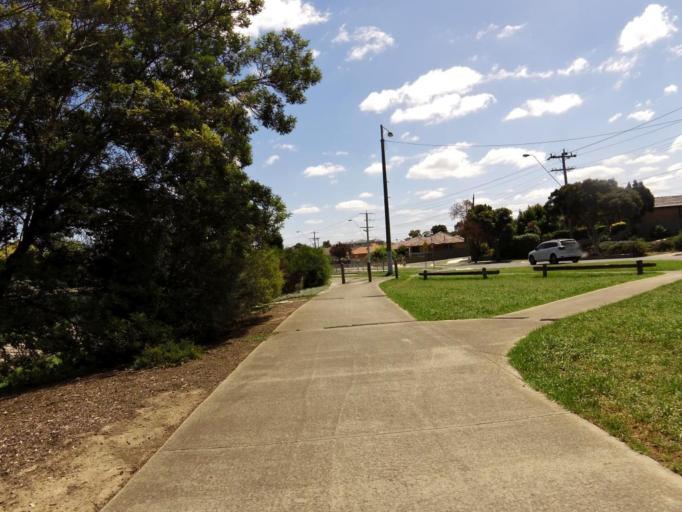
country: AU
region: Victoria
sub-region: Whittlesea
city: Lalor
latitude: -37.6714
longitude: 145.0102
